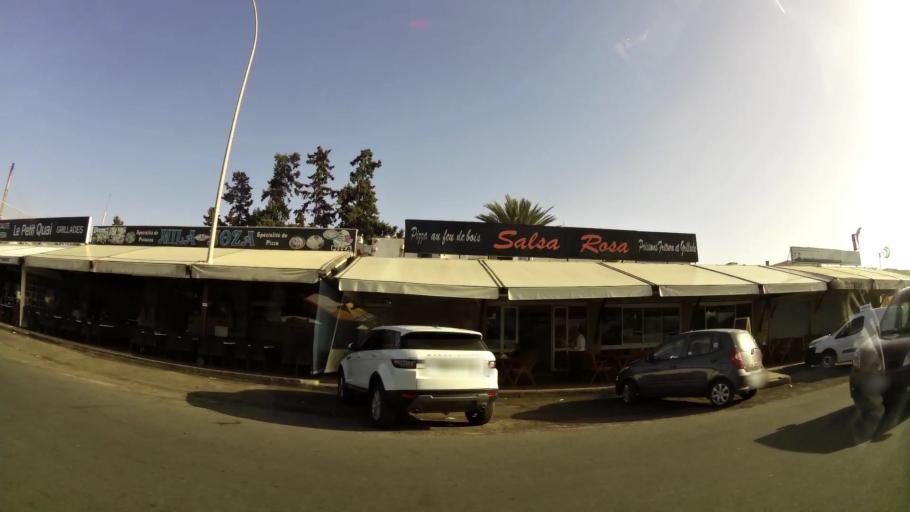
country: MA
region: Souss-Massa-Draa
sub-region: Agadir-Ida-ou-Tnan
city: Agadir
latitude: 30.4266
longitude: -9.5880
